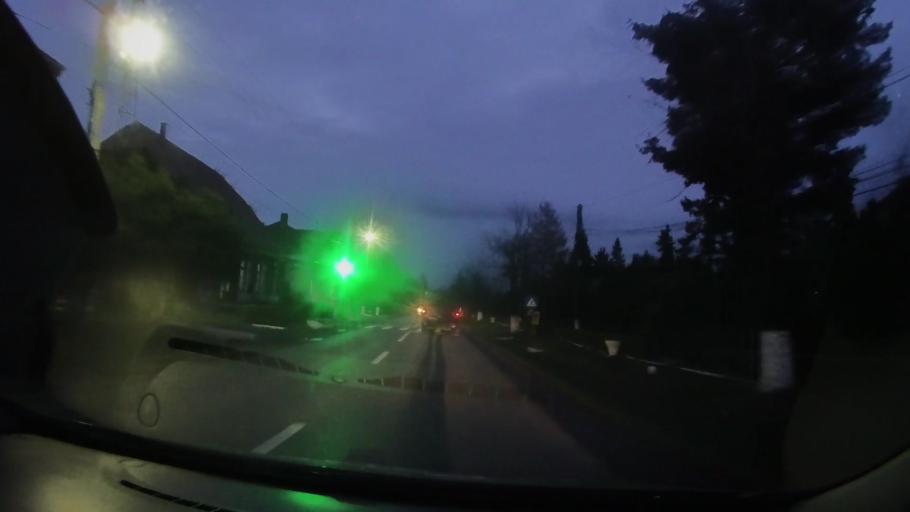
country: RO
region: Mures
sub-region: Comuna Gurghiu
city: Gurghiu
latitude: 46.7720
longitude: 24.8598
